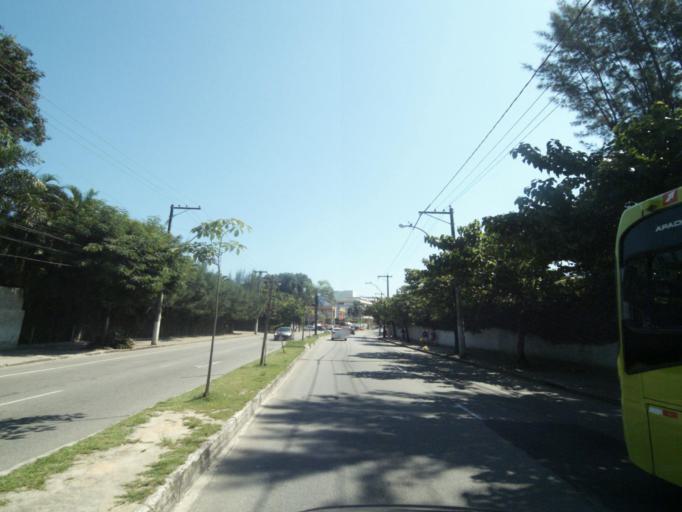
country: BR
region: Rio de Janeiro
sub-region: Niteroi
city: Niteroi
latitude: -22.9059
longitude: -43.0538
